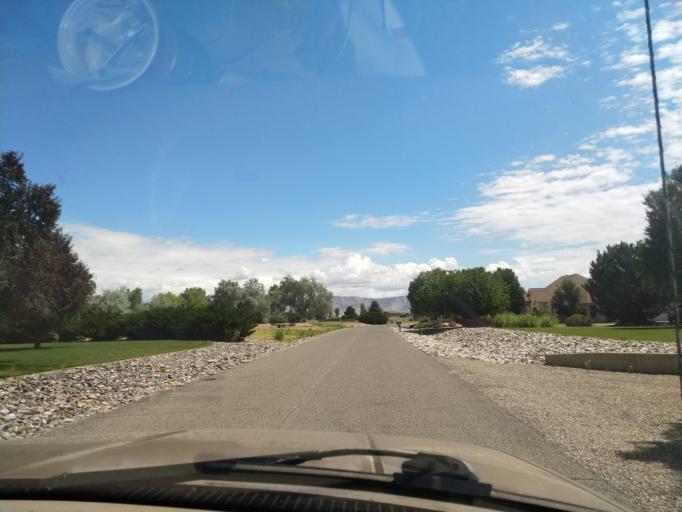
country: US
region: Colorado
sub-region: Mesa County
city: Redlands
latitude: 39.1453
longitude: -108.6044
